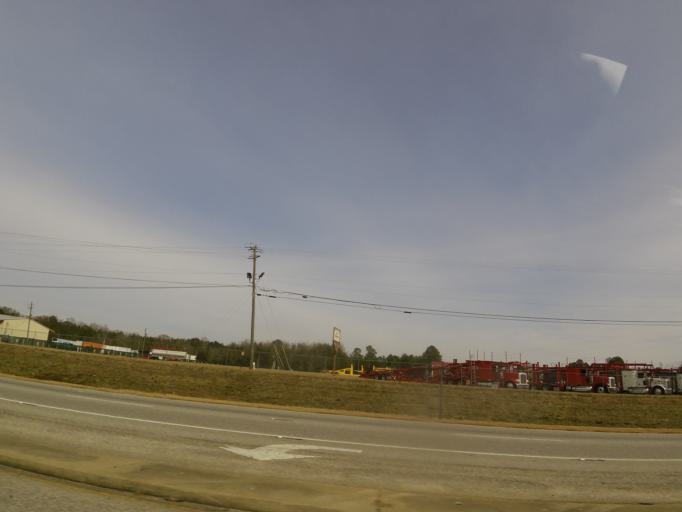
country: US
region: Alabama
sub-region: Dale County
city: Newton
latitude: 31.3773
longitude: -85.5704
